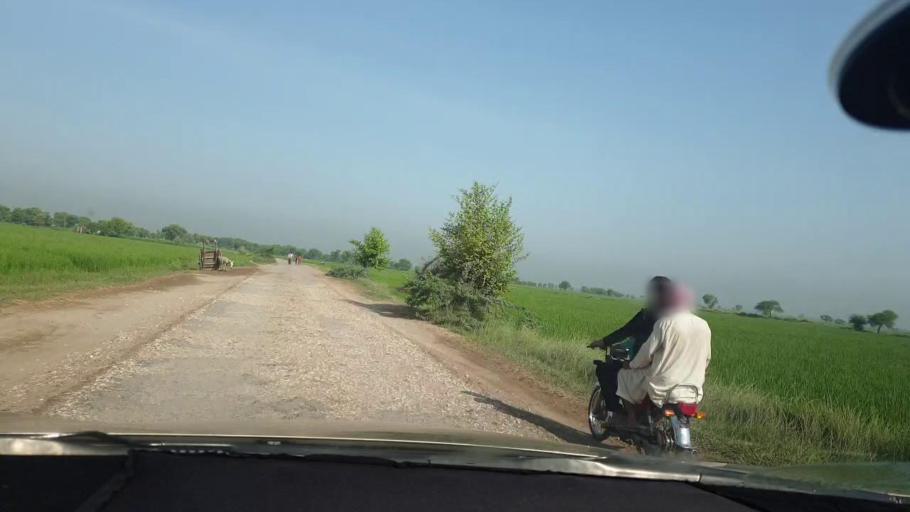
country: PK
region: Sindh
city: Kambar
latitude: 27.6574
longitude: 68.0267
